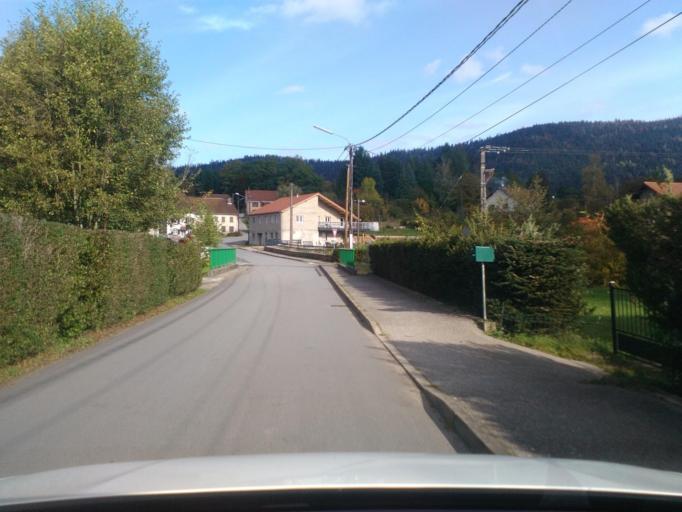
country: FR
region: Lorraine
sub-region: Departement des Vosges
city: Senones
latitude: 48.4122
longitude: 7.0425
